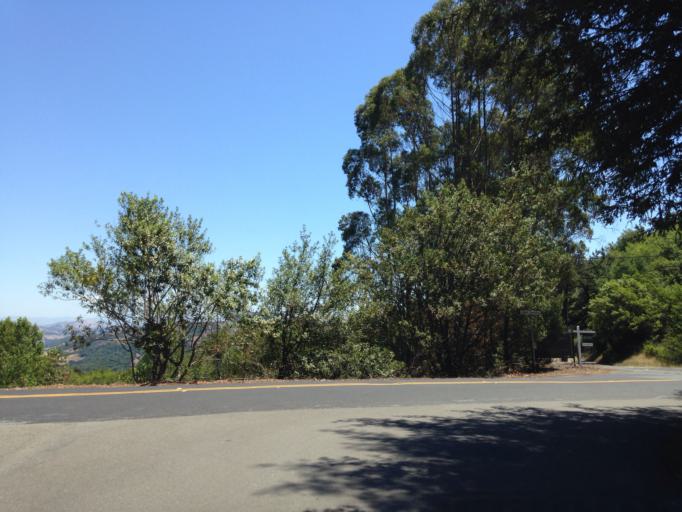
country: US
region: California
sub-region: Contra Costa County
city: Orinda
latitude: 37.8799
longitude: -122.2217
